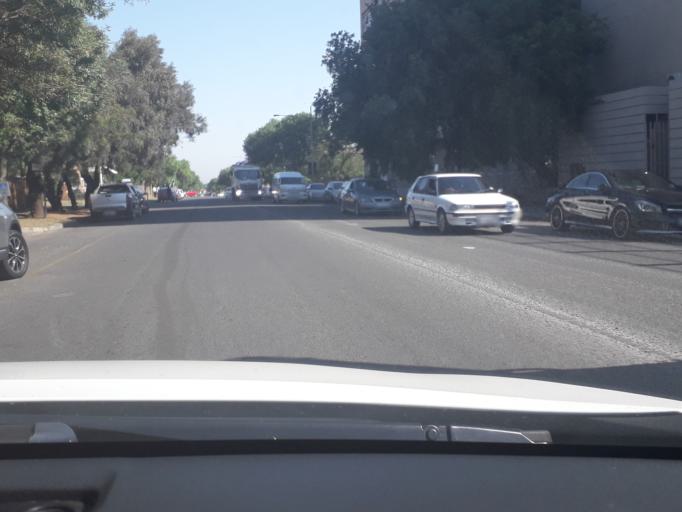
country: ZA
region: Gauteng
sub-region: Ekurhuleni Metropolitan Municipality
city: Benoni
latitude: -26.1955
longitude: 28.3078
